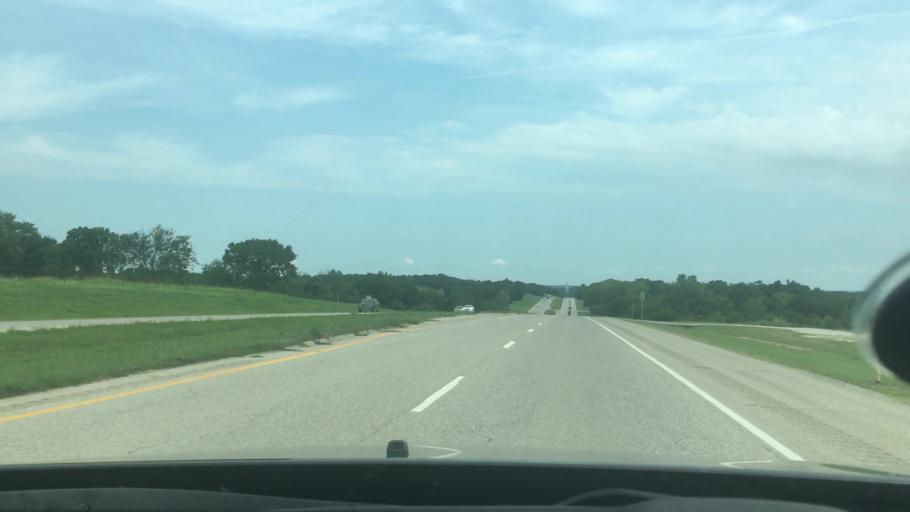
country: US
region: Oklahoma
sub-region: Seminole County
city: Seminole
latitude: 35.1971
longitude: -96.6749
